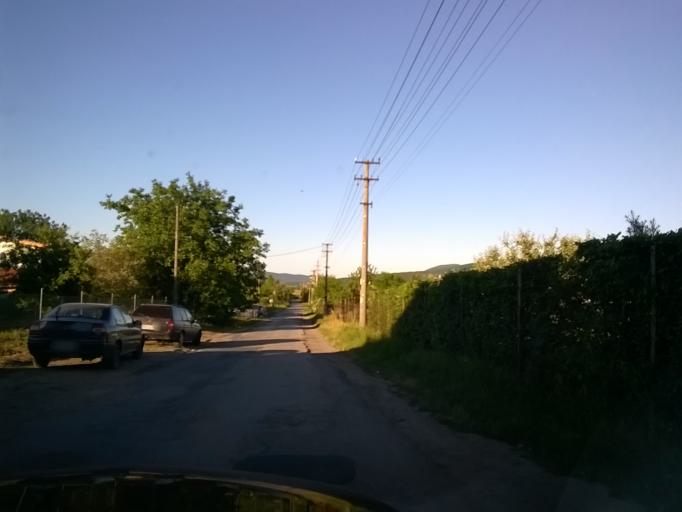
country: SK
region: Nitriansky
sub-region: Okres Nitra
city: Nitra
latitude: 48.3526
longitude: 18.0253
